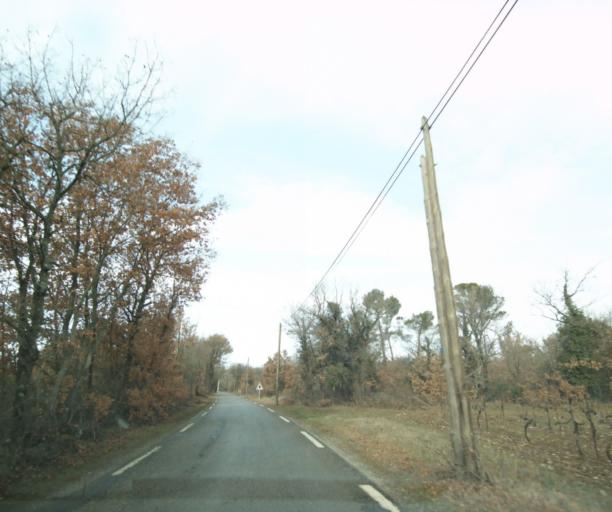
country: FR
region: Provence-Alpes-Cote d'Azur
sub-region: Departement du Var
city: Rougiers
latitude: 43.4014
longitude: 5.8812
